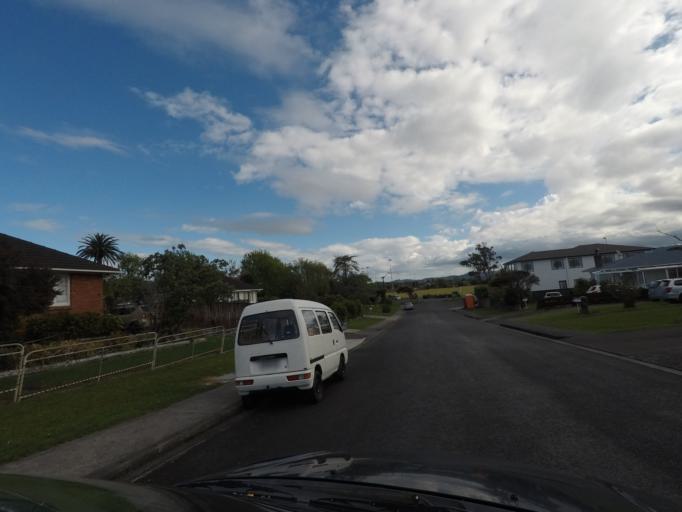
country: NZ
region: Auckland
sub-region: Auckland
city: Rosebank
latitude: -36.8709
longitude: 174.6441
